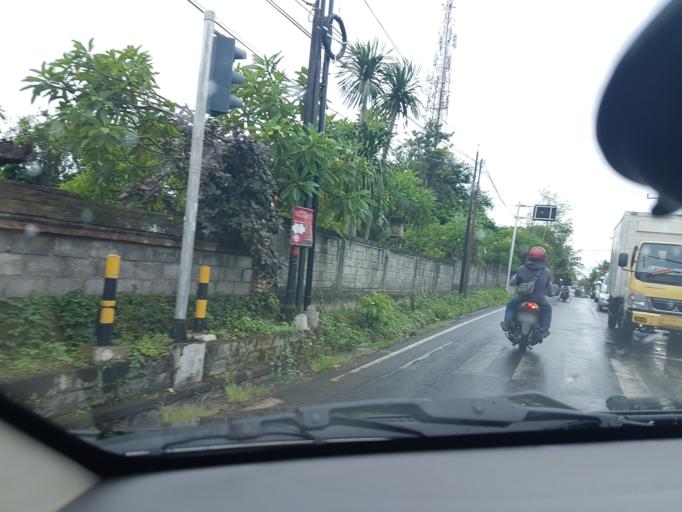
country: ID
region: Bali
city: Banjar Desa
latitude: -8.5799
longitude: 115.2391
